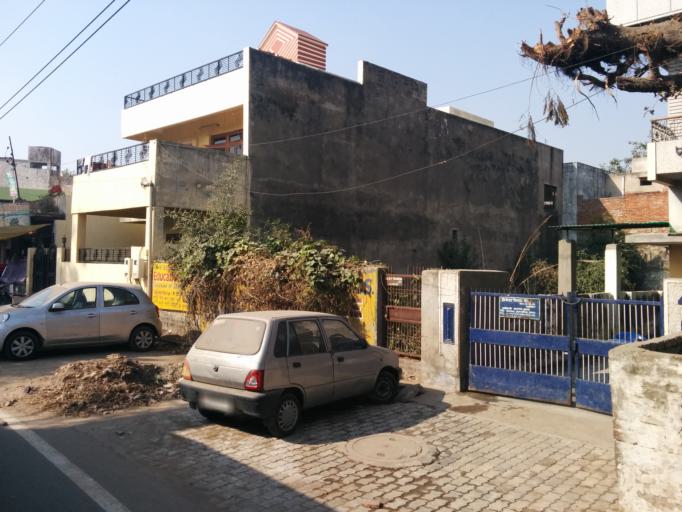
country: IN
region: Uttar Pradesh
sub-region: Agra
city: Agra
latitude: 27.1802
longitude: 77.9779
